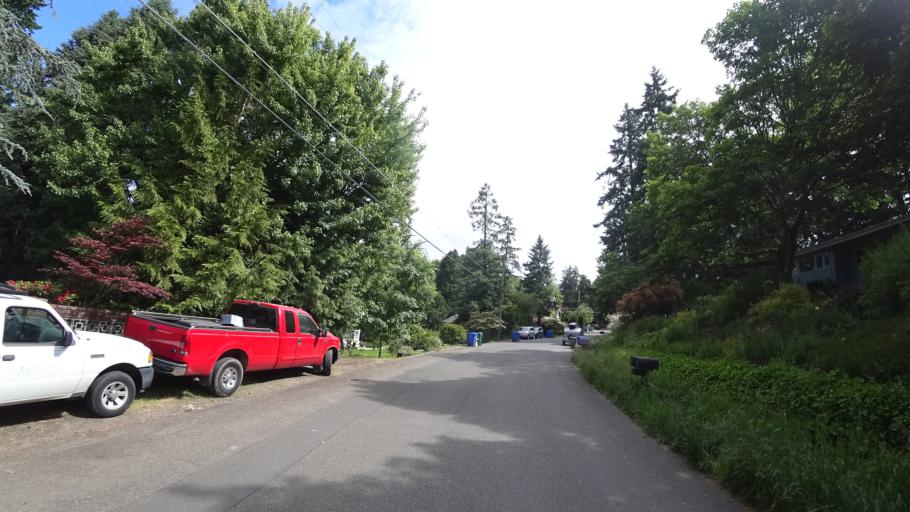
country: US
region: Oregon
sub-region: Clackamas County
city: Lake Oswego
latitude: 45.4579
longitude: -122.6888
